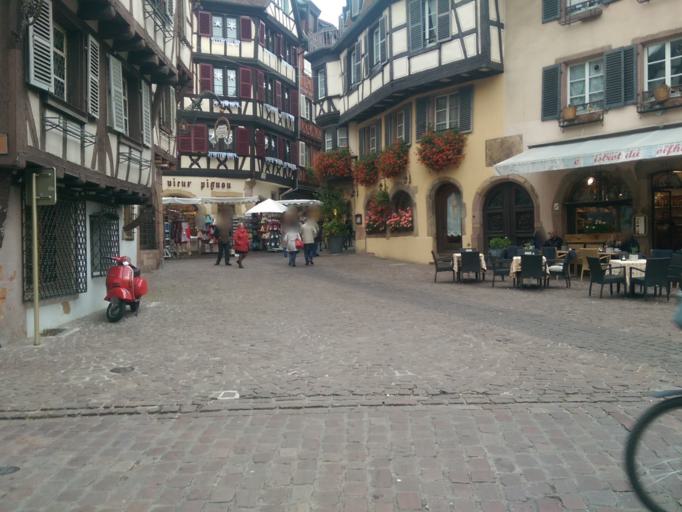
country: FR
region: Alsace
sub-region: Departement du Haut-Rhin
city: Colmar
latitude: 48.0761
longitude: 7.3589
